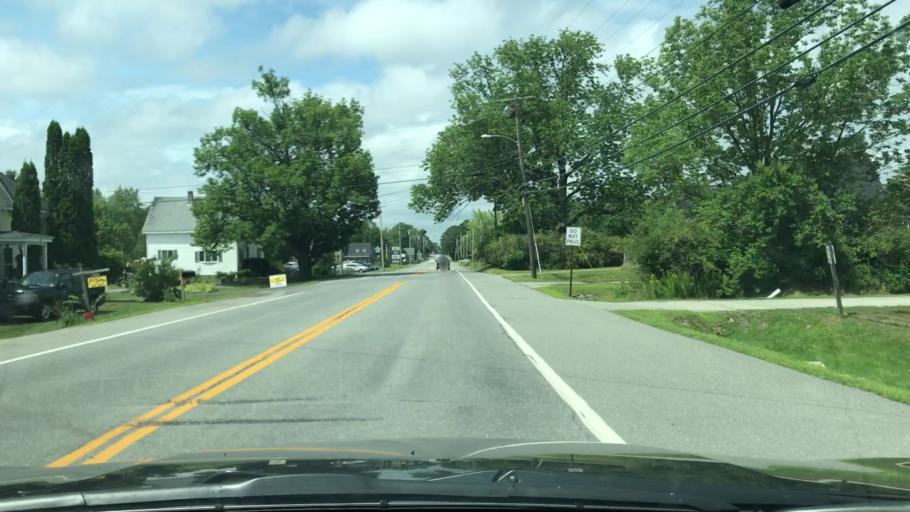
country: US
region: Maine
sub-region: Waldo County
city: Belfast
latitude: 44.4004
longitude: -68.9879
